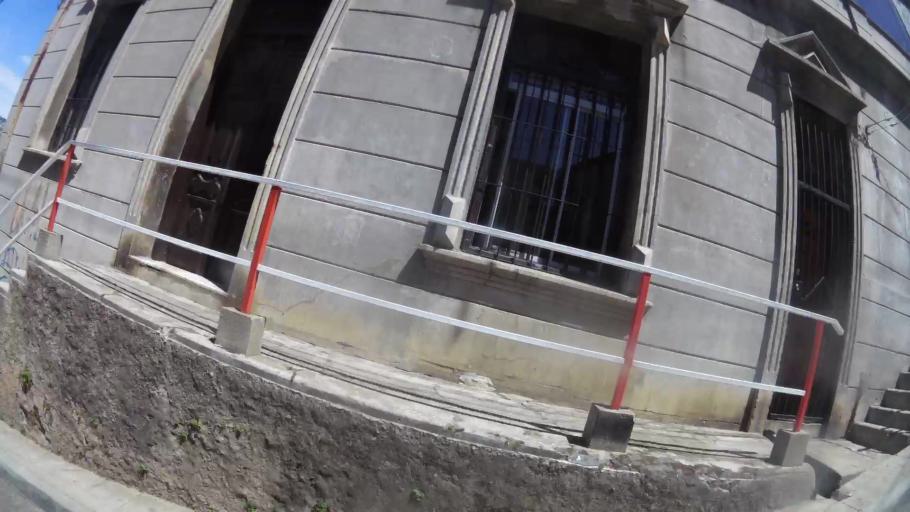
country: CL
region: Valparaiso
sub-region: Provincia de Valparaiso
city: Valparaiso
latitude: -33.0502
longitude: -71.5973
